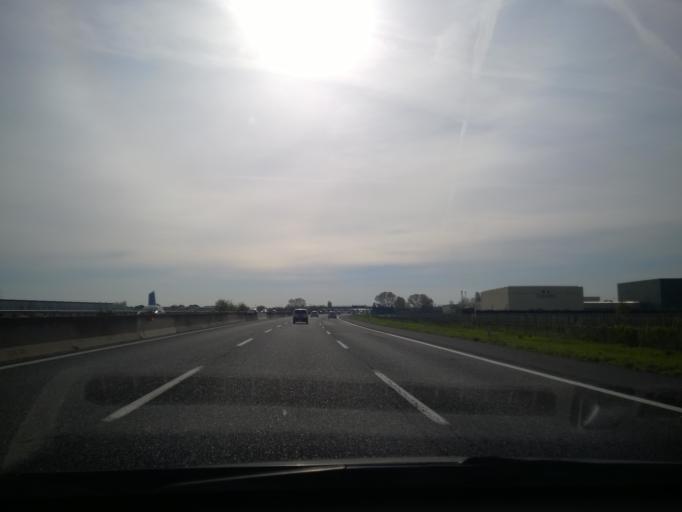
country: IT
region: Emilia-Romagna
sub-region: Forli-Cesena
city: Forli
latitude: 44.2594
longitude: 12.0719
